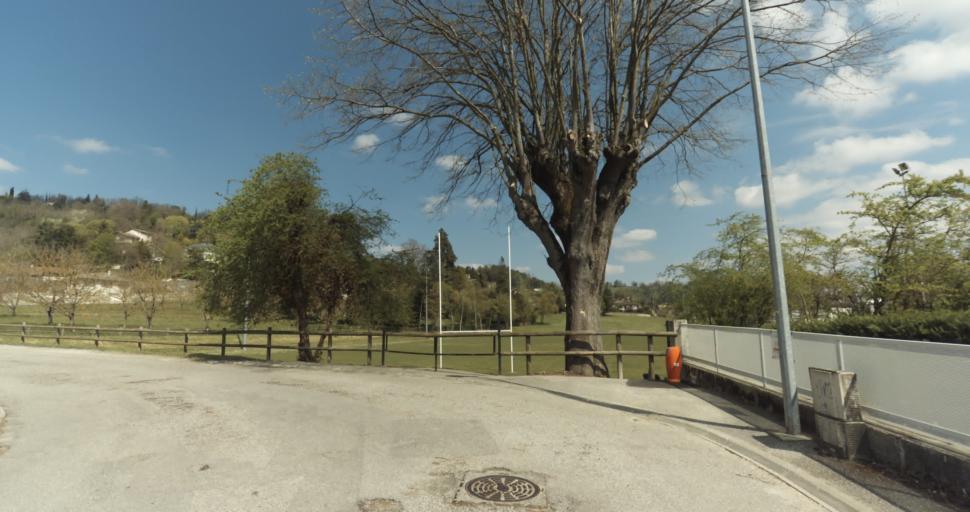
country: FR
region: Rhone-Alpes
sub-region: Departement de l'Isere
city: Saint-Marcellin
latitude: 45.1567
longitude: 5.3149
